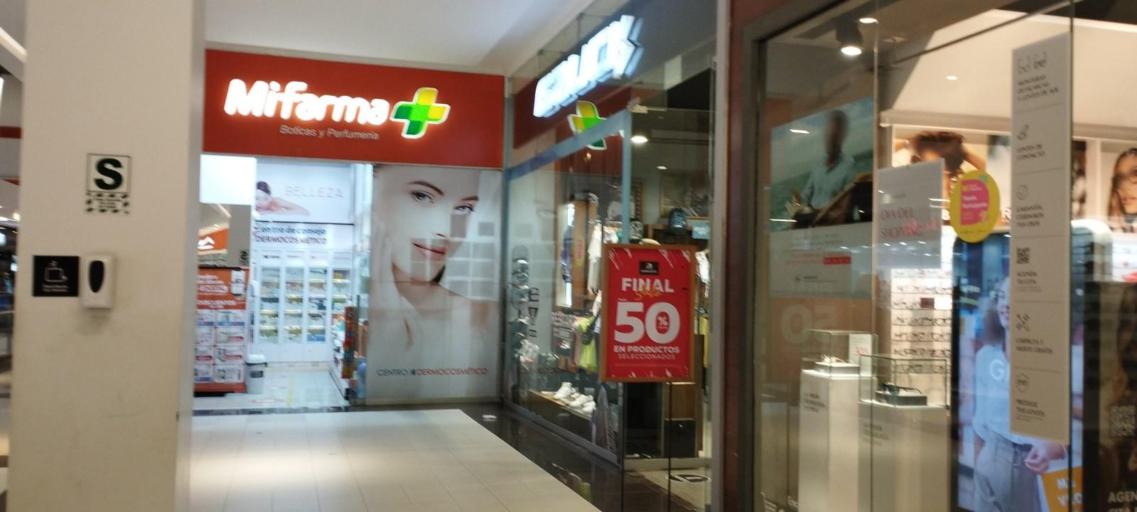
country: PE
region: Cusco
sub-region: Provincia de Cusco
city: Cusco
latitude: -13.5229
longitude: -71.9502
